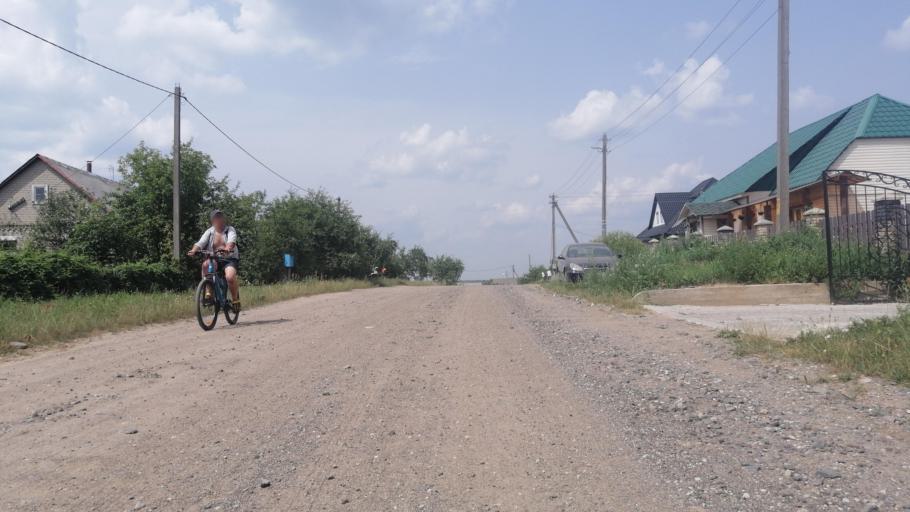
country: BY
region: Grodnenskaya
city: Navahrudak
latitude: 53.6069
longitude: 25.8274
